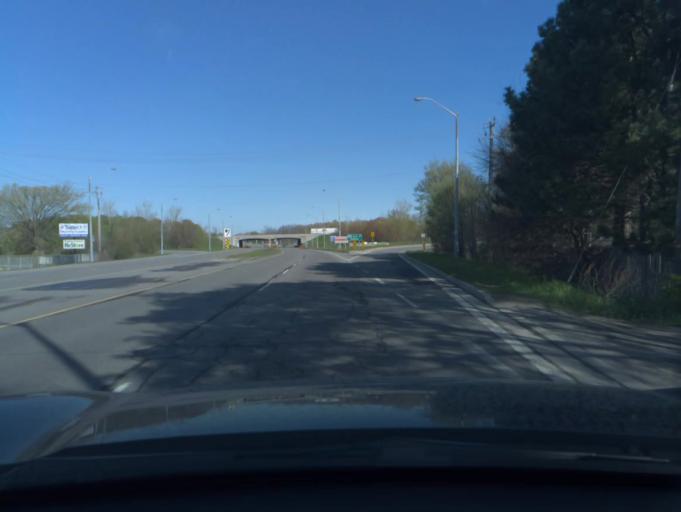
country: CA
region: Ontario
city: North Perth
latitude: 43.8000
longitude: -80.9999
